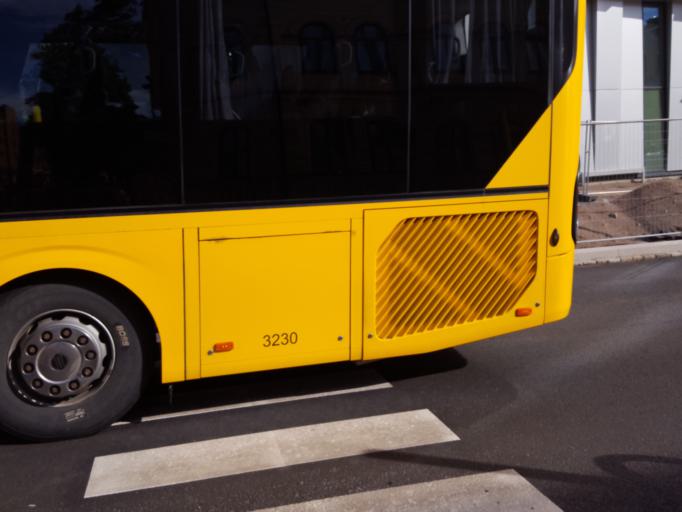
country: SE
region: Uppsala
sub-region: Uppsala Kommun
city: Uppsala
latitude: 59.8616
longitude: 17.6458
